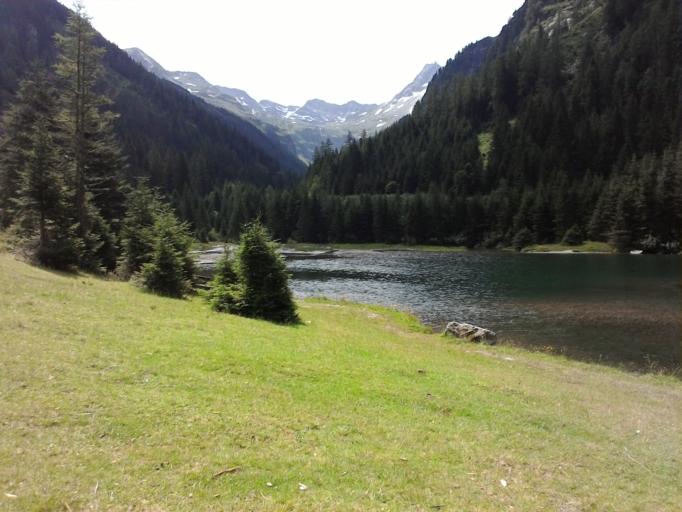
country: AT
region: Salzburg
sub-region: Politischer Bezirk Zell am See
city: Stuhlfelden
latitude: 47.1786
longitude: 12.5299
